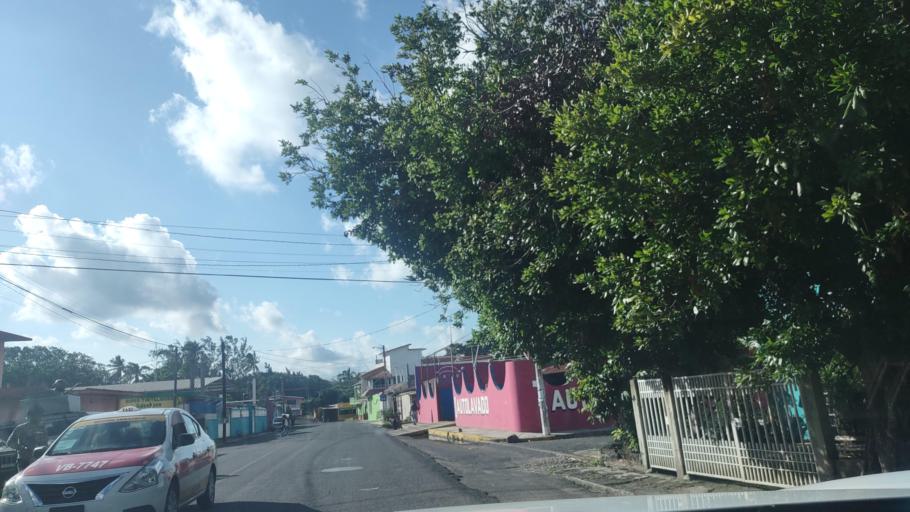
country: MX
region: Veracruz
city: El Tejar
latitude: 19.0693
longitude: -96.1603
